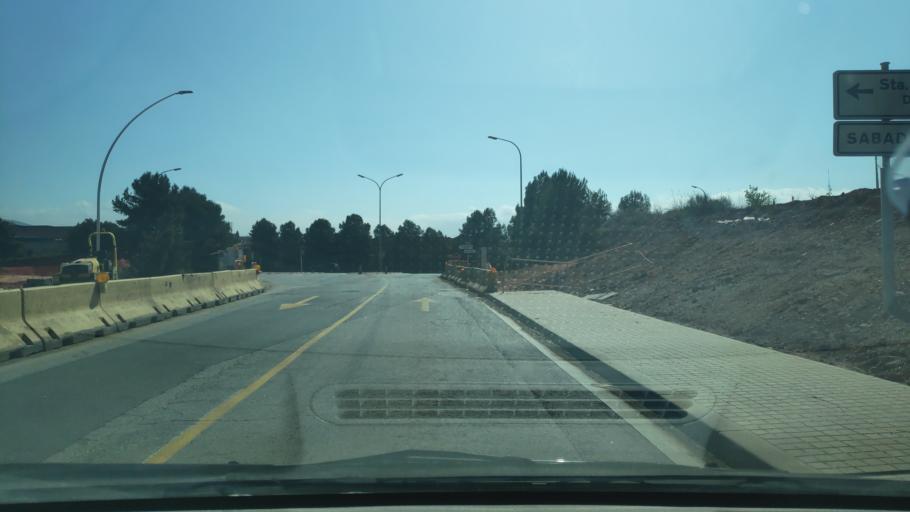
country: ES
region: Catalonia
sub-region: Provincia de Barcelona
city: Barbera del Valles
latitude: 41.5318
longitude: 2.1338
